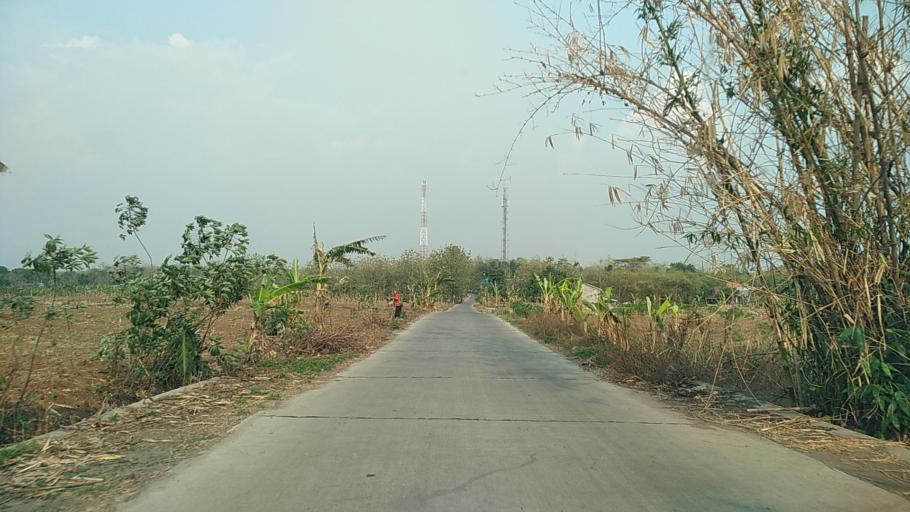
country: ID
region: Central Java
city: Mranggen
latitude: -7.0658
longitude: 110.4944
